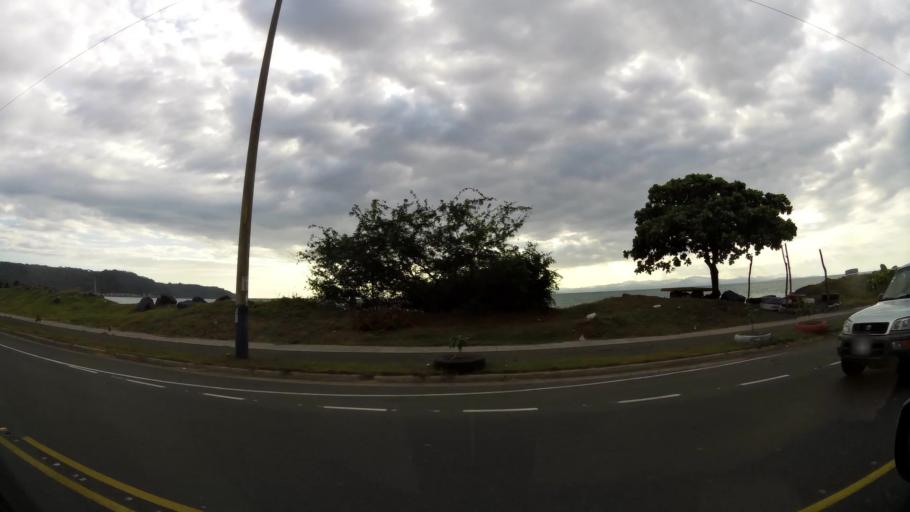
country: CR
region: Puntarenas
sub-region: Canton Central de Puntarenas
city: Chacarita
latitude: 9.9296
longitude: -84.7180
